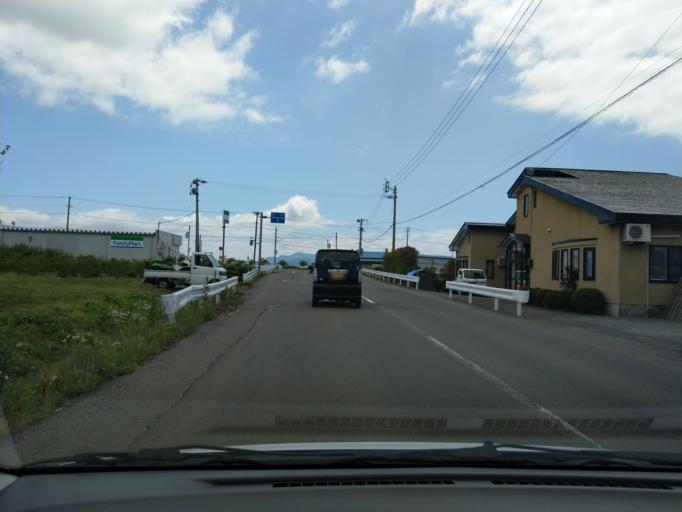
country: JP
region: Aomori
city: Kuroishi
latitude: 40.6373
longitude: 140.5674
